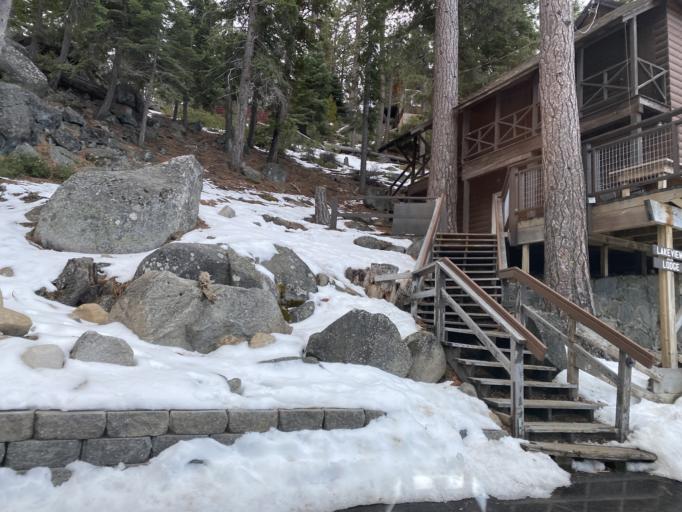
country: US
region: Nevada
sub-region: Douglas County
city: Kingsbury
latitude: 39.0027
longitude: -119.9574
